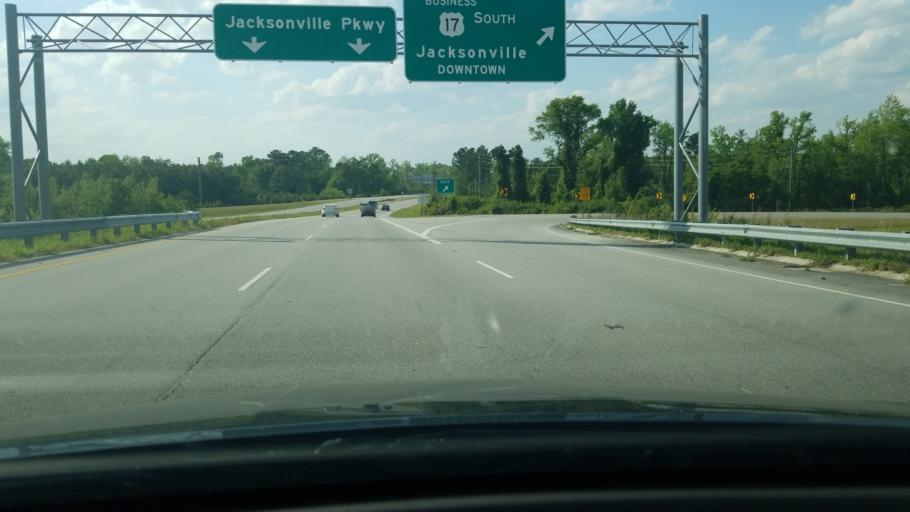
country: US
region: North Carolina
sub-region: Onslow County
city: Pumpkin Center
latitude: 34.7740
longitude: -77.3984
